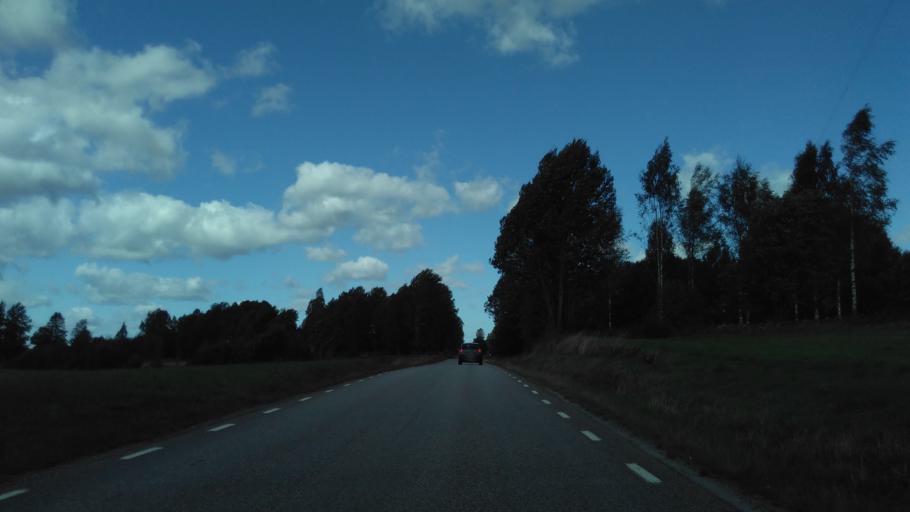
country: SE
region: Vaestra Goetaland
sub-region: Herrljunga Kommun
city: Herrljunga
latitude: 58.1456
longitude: 13.0218
